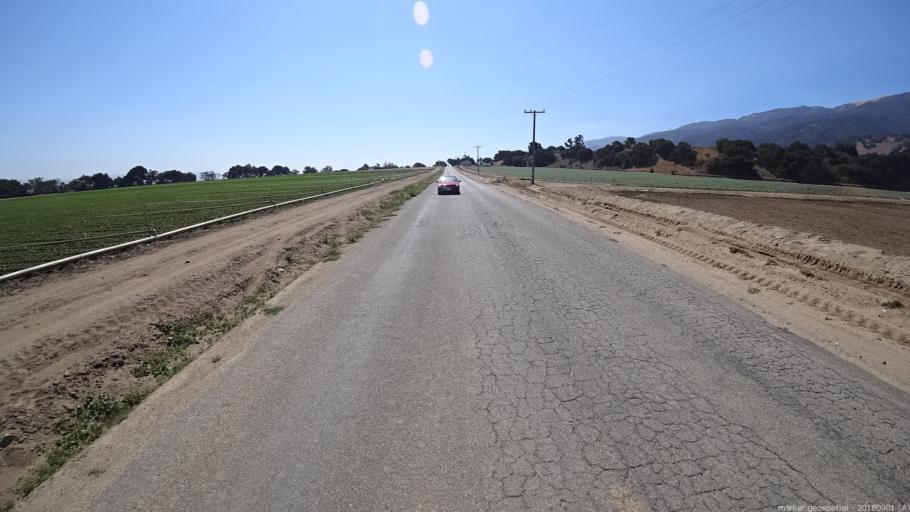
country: US
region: California
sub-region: Monterey County
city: Chualar
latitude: 36.5264
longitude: -121.5257
